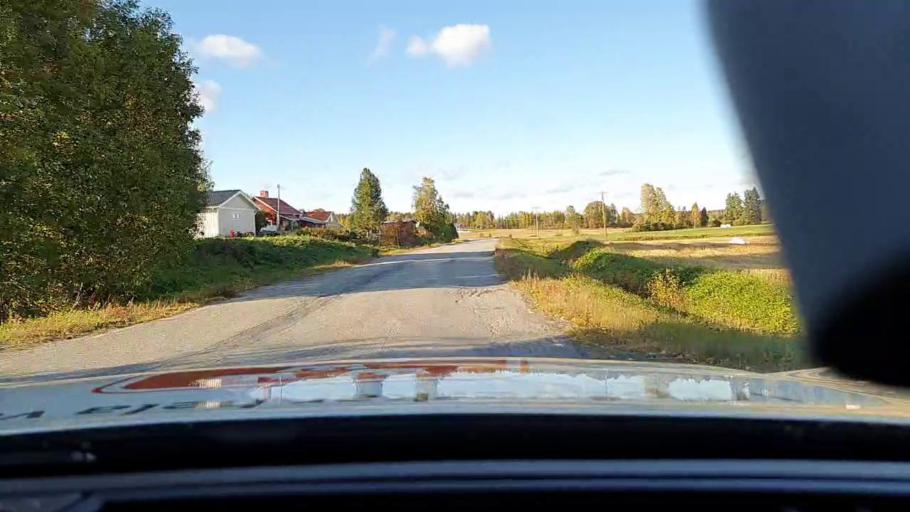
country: SE
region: Norrbotten
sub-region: Pitea Kommun
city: Norrfjarden
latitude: 65.5219
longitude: 21.4927
